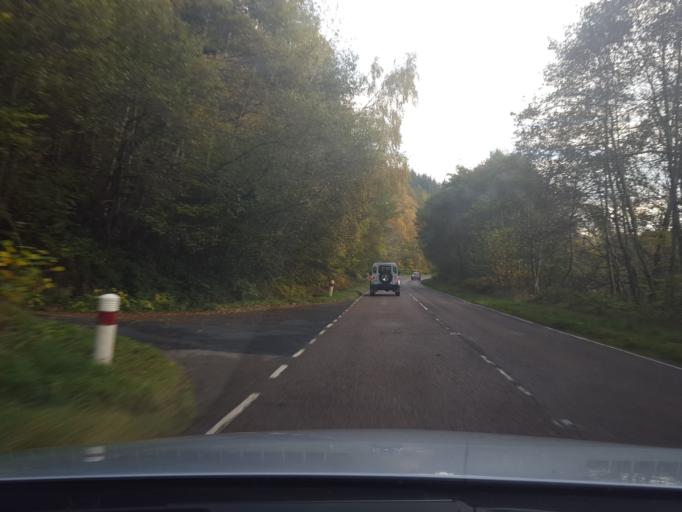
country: GB
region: Scotland
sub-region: Highland
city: Beauly
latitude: 57.2210
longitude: -4.6378
